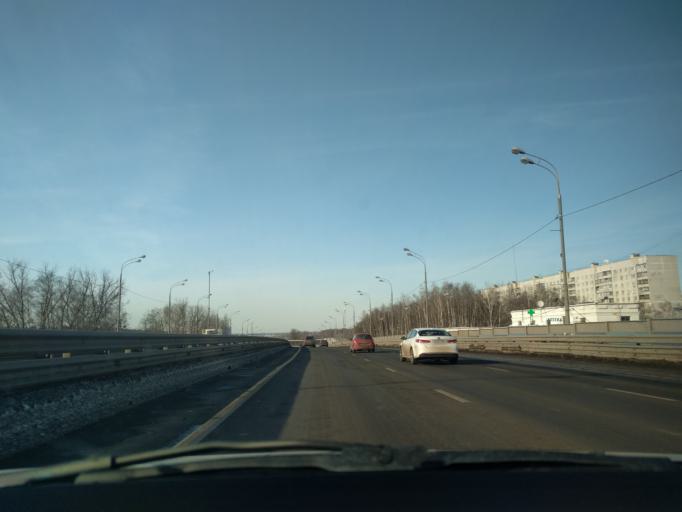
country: RU
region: Moscow
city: Severnyy
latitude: 55.9317
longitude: 37.5473
